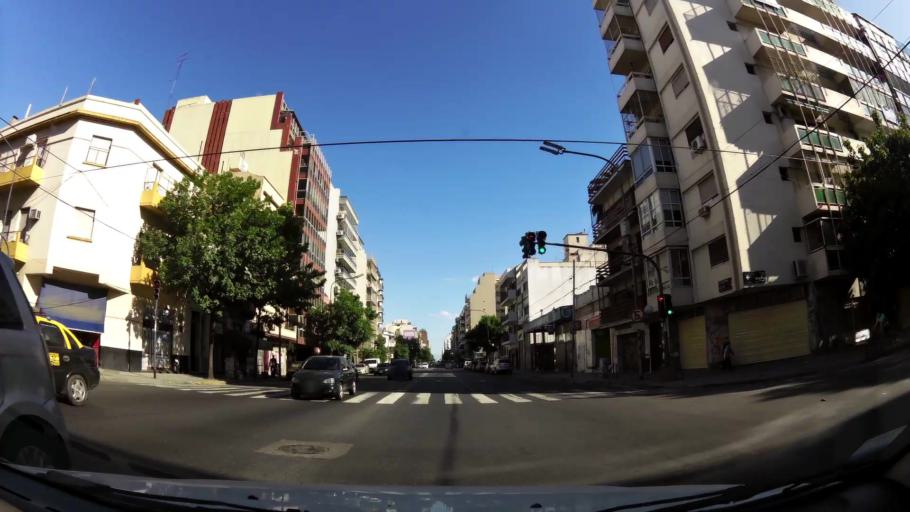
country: AR
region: Buenos Aires F.D.
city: Villa Santa Rita
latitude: -34.6242
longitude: -58.4726
